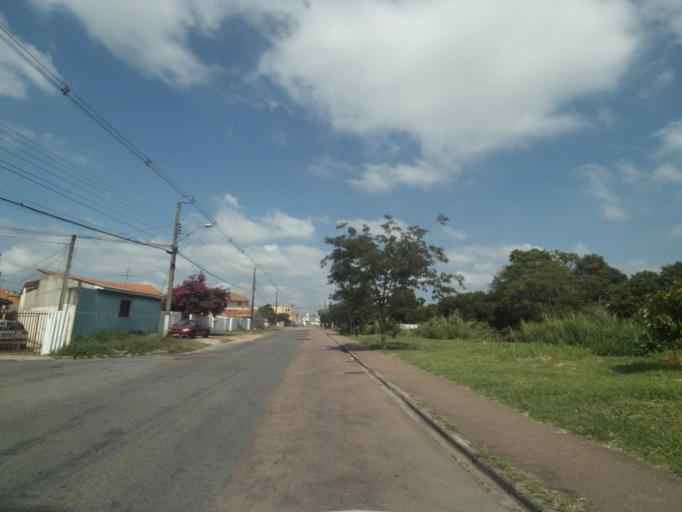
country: BR
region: Parana
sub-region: Sao Jose Dos Pinhais
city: Sao Jose dos Pinhais
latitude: -25.5357
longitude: -49.2589
